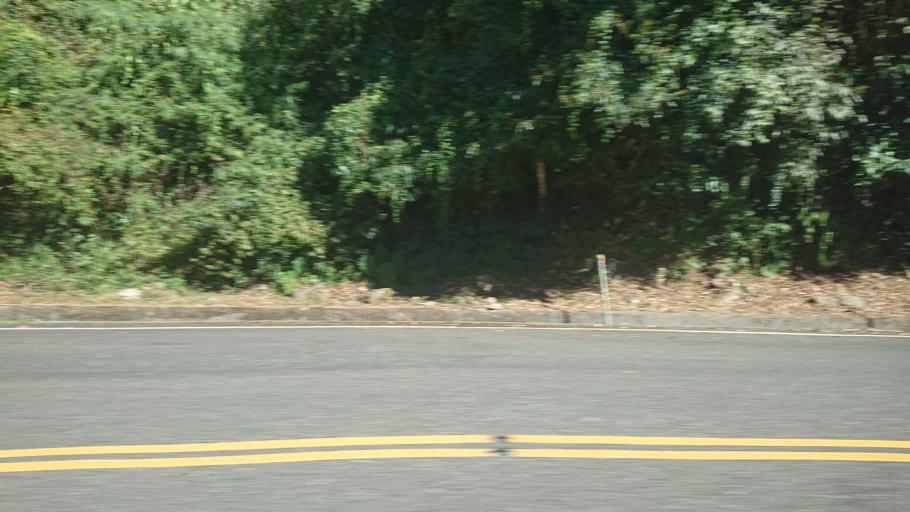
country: TW
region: Taiwan
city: Lugu
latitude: 23.4829
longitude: 120.7385
